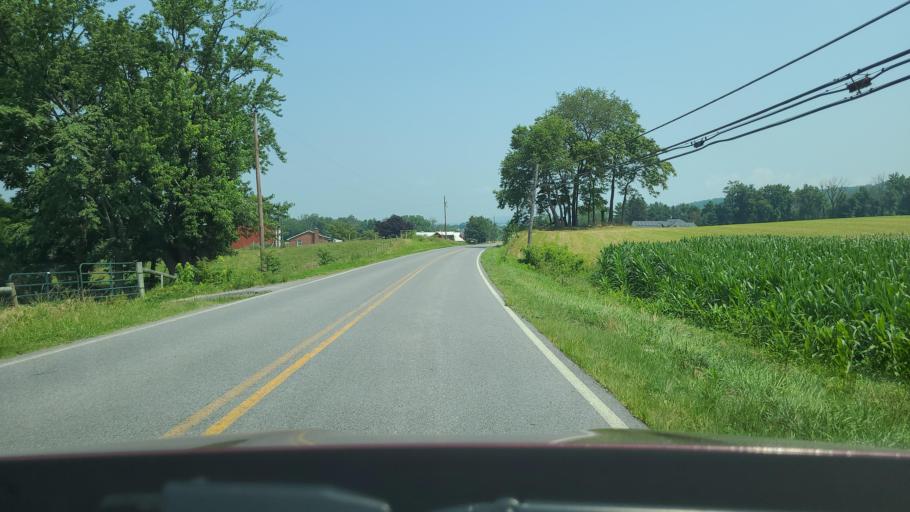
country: US
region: Maryland
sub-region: Frederick County
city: Jefferson
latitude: 39.3729
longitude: -77.5236
